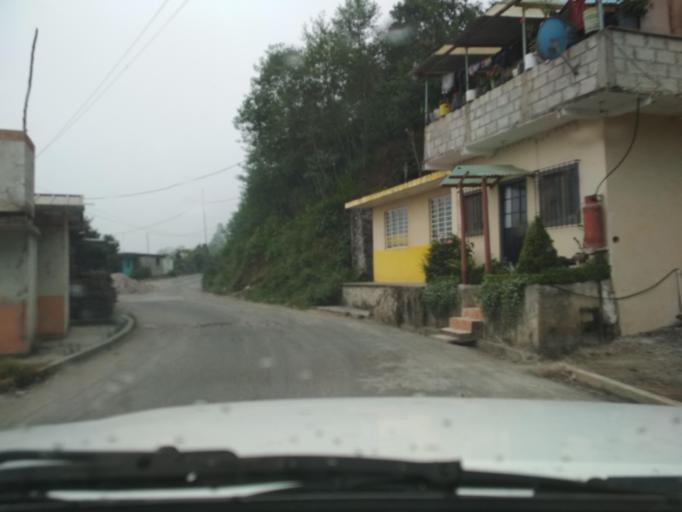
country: MX
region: Veracruz
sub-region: La Perla
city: Metlac Hernandez (Metlac Primero)
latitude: 18.9510
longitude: -97.1659
